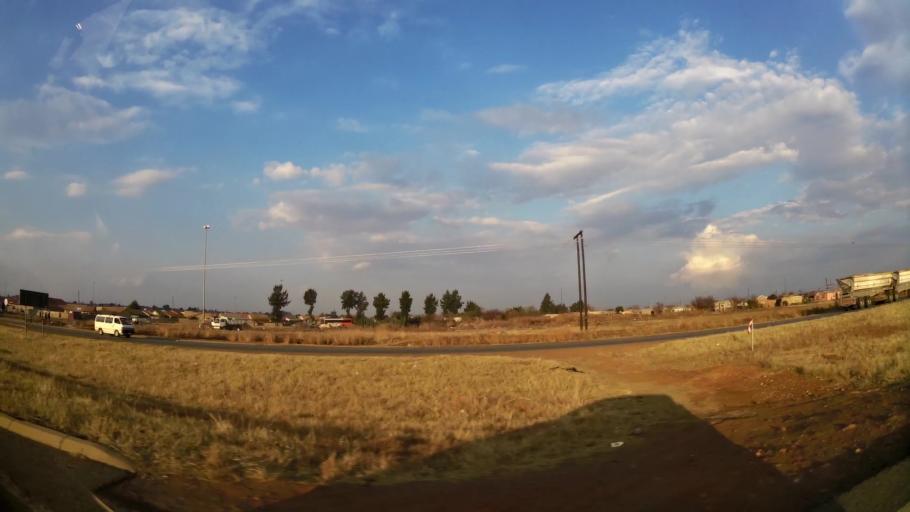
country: ZA
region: Gauteng
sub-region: City of Johannesburg Metropolitan Municipality
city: Orange Farm
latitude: -26.5914
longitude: 27.8211
